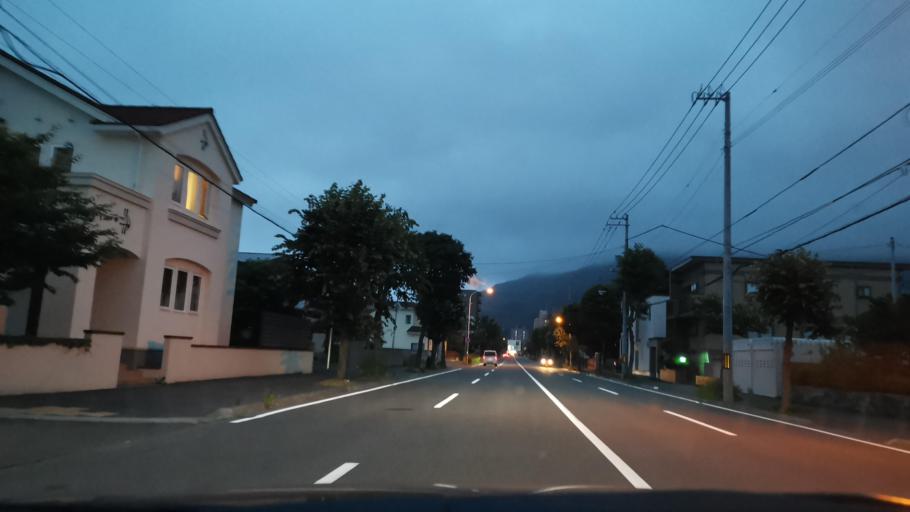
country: JP
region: Hokkaido
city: Sapporo
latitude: 43.0438
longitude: 141.3326
